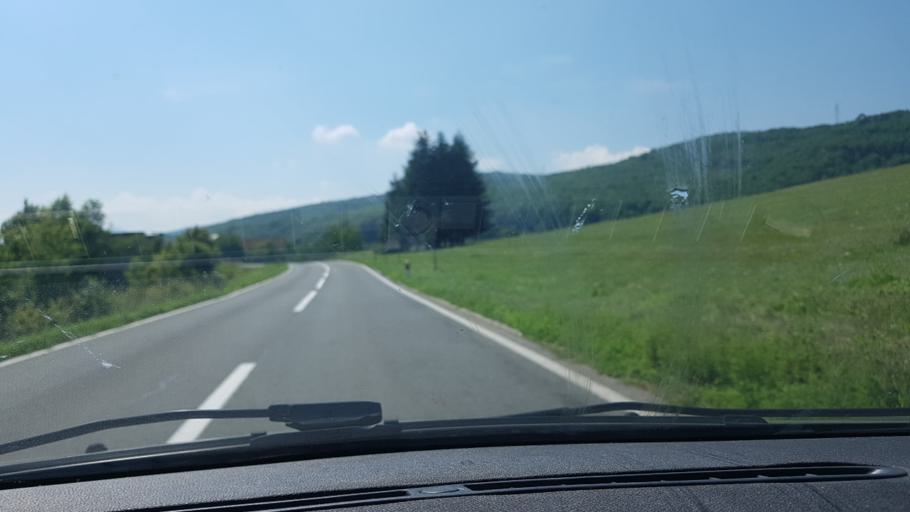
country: HR
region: Licko-Senjska
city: Otocac
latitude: 44.8884
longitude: 15.1923
